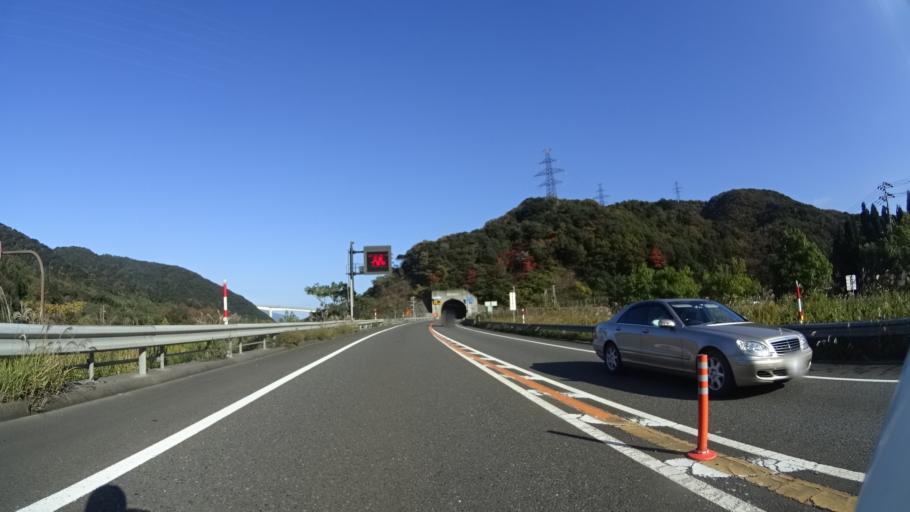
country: JP
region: Fukui
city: Tsuruga
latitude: 35.6141
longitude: 136.0839
